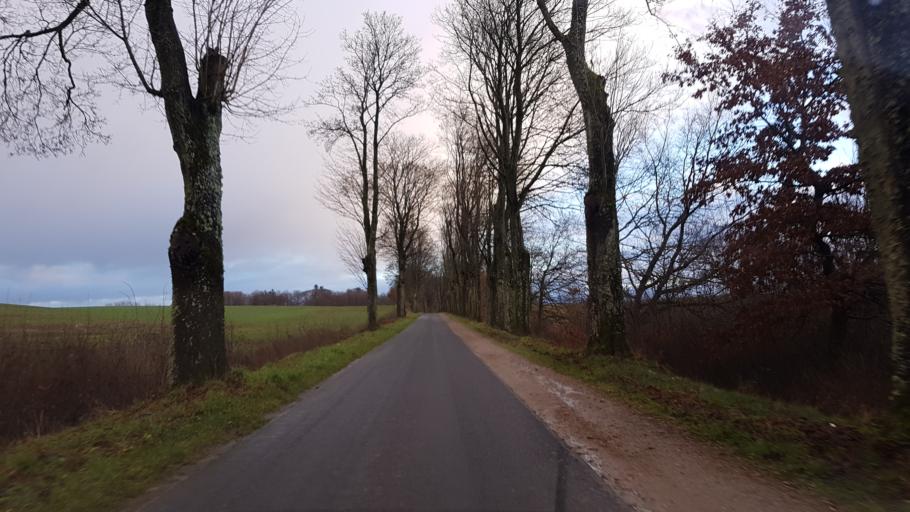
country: PL
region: West Pomeranian Voivodeship
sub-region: Powiat bialogardzki
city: Karlino
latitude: 53.9501
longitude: 15.9078
